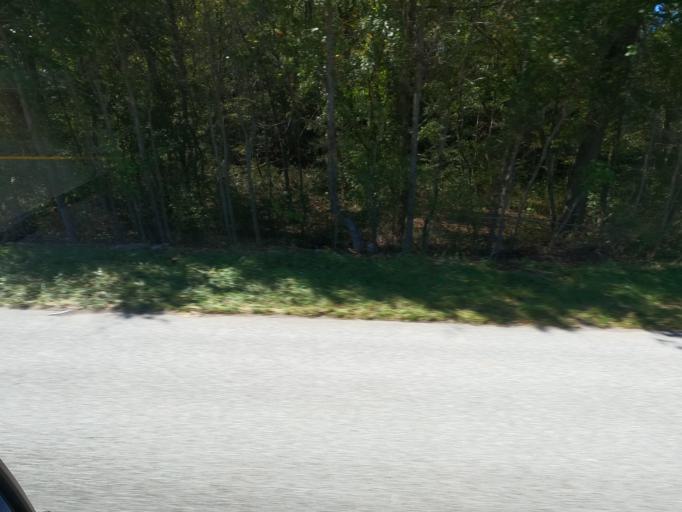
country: US
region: Tennessee
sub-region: Maury County
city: Mount Pleasant
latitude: 35.3951
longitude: -87.2779
